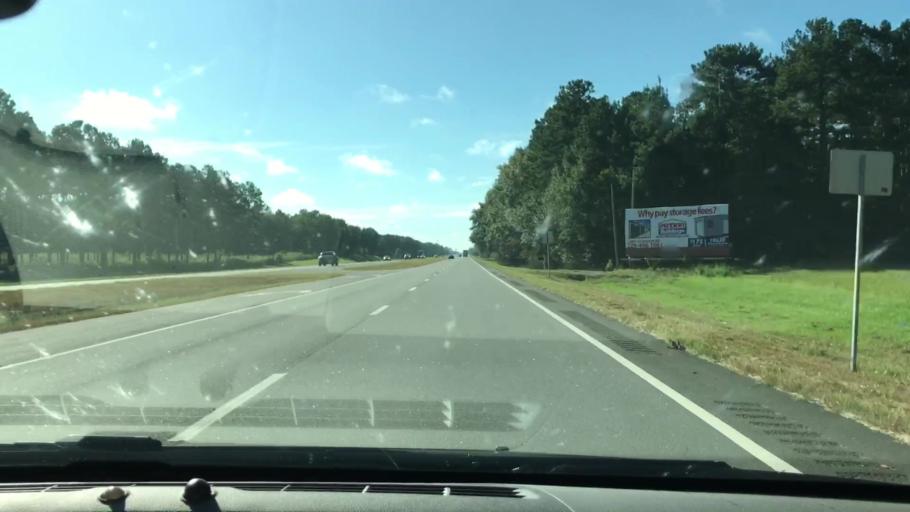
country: US
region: Georgia
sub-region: Lee County
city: Leesburg
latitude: 31.6796
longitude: -84.2990
